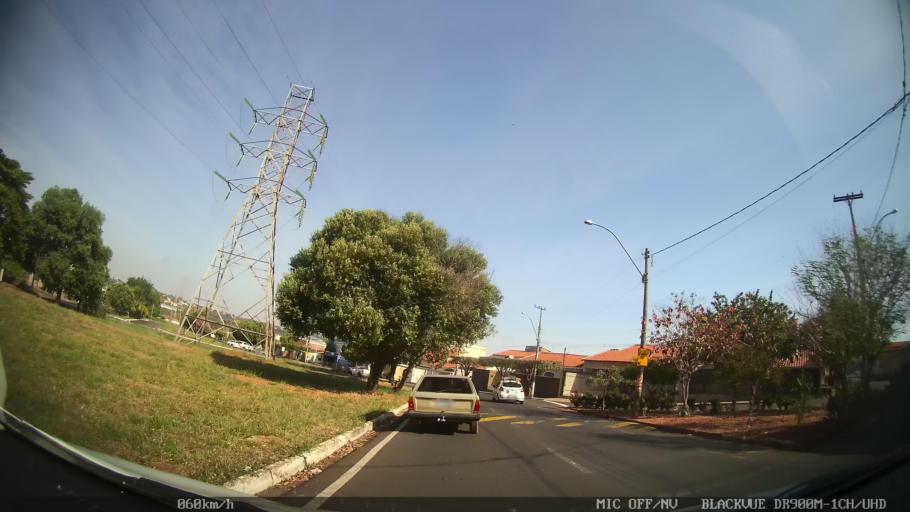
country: BR
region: Sao Paulo
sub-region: Sao Jose Do Rio Preto
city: Sao Jose do Rio Preto
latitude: -20.7975
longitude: -49.4174
